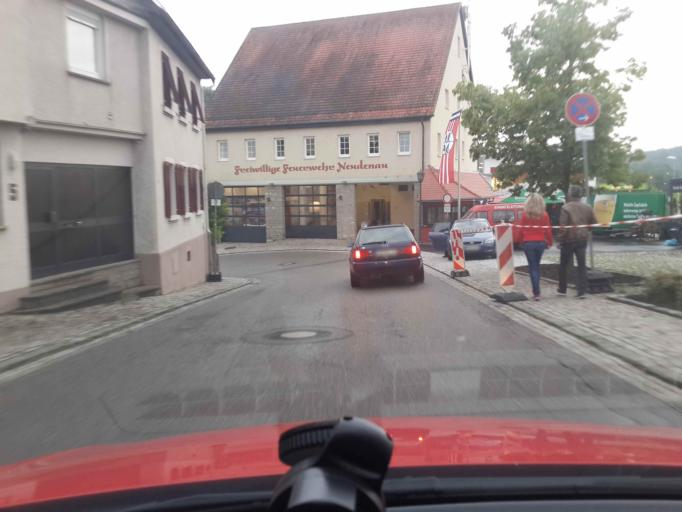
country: DE
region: Baden-Wuerttemberg
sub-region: Regierungsbezirk Stuttgart
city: Neudenau
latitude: 49.2903
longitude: 9.2692
